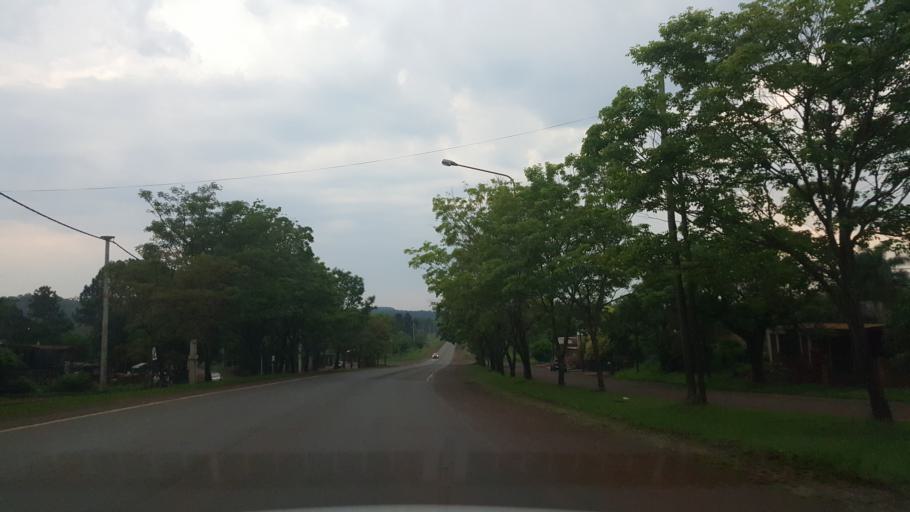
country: AR
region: Misiones
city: Jardin America
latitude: -27.0339
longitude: -55.2237
